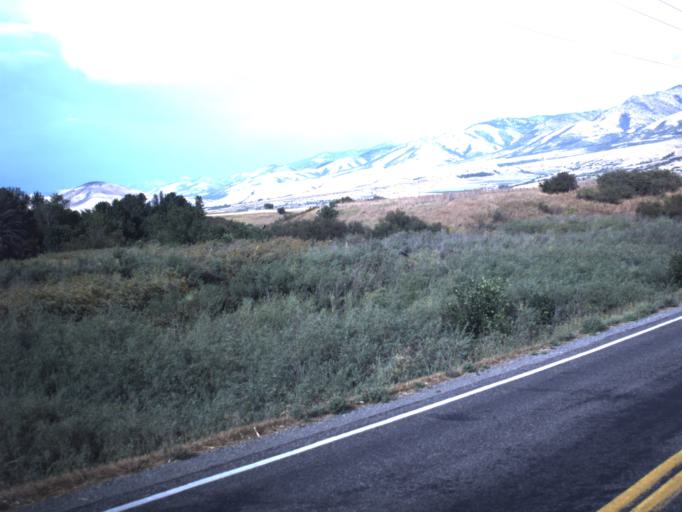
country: US
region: Utah
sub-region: Cache County
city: Lewiston
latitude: 41.9761
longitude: -111.8290
